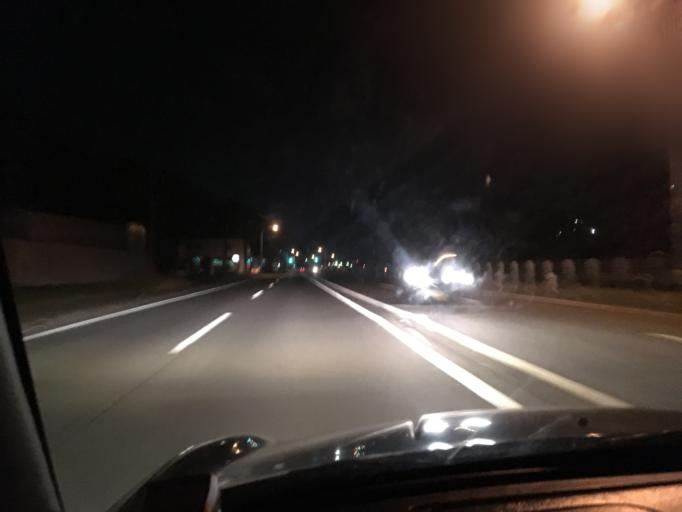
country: JP
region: Hokkaido
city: Muroran
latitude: 42.3547
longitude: 140.9899
